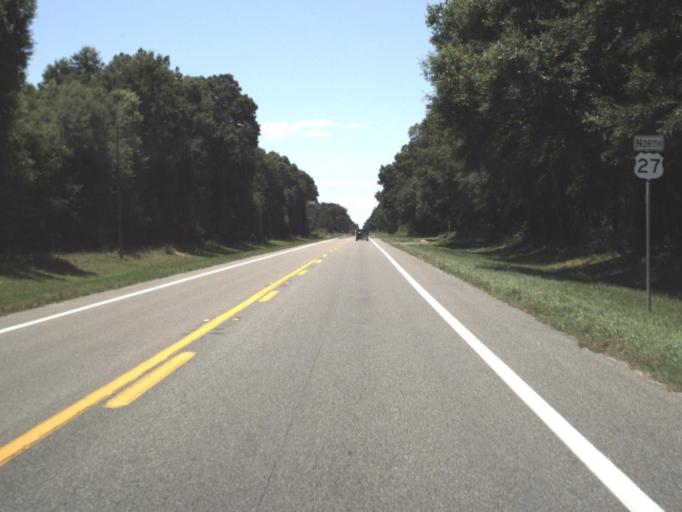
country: US
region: Florida
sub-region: Lafayette County
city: Mayo
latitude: 29.9660
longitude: -82.9755
